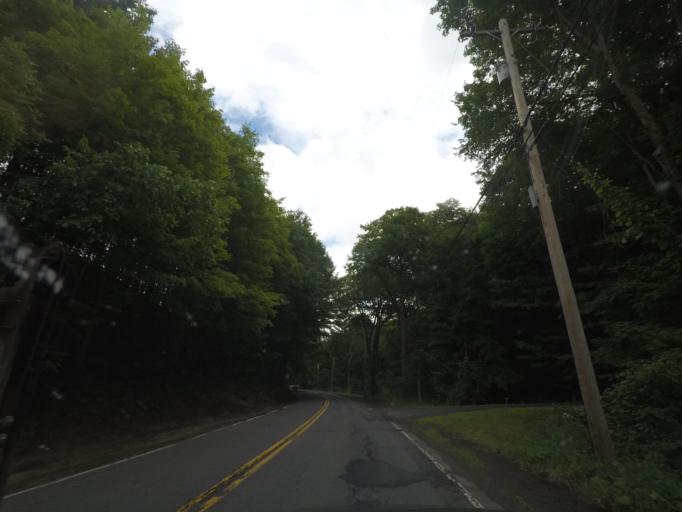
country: US
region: New York
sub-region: Rensselaer County
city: West Sand Lake
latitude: 42.6698
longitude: -73.6150
